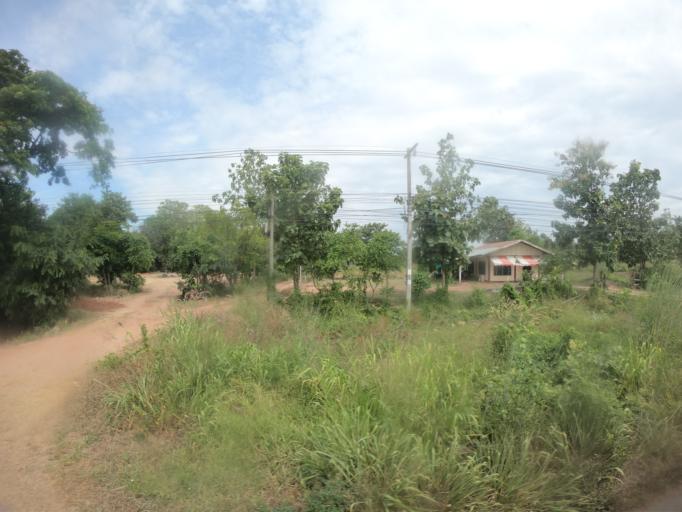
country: TH
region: Maha Sarakham
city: Chiang Yuen
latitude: 16.3437
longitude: 103.1317
